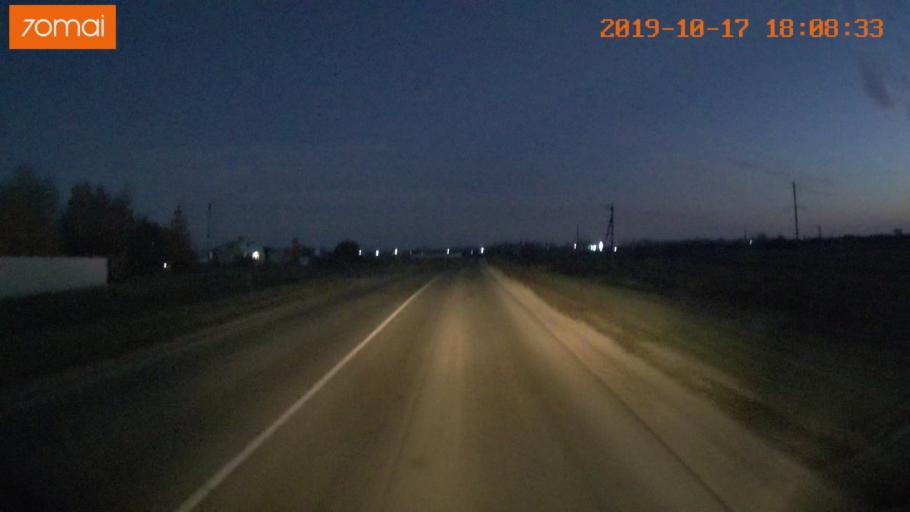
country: RU
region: Tula
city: Kurkino
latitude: 53.4327
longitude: 38.6441
